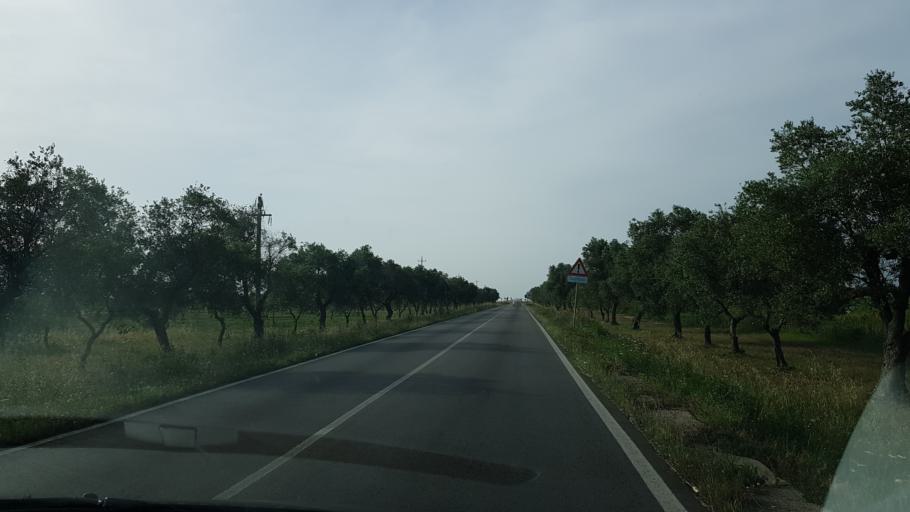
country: IT
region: Apulia
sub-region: Provincia di Brindisi
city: San Pancrazio Salentino
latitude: 40.3726
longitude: 17.8389
